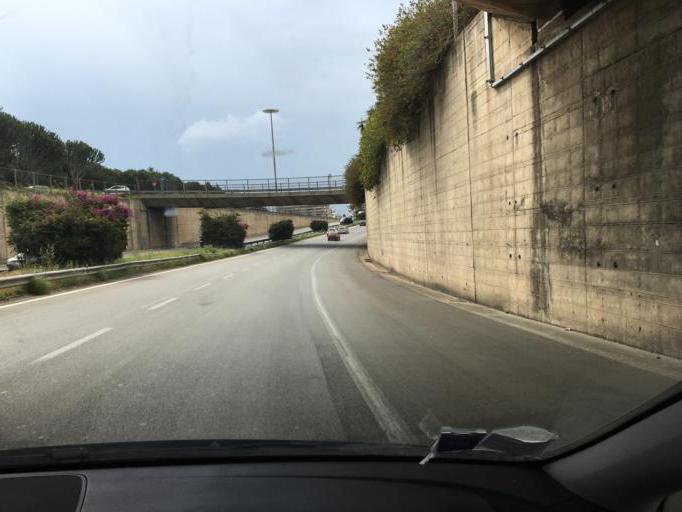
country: IT
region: Sicily
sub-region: Palermo
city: Palermo
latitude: 38.1490
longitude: 13.3259
